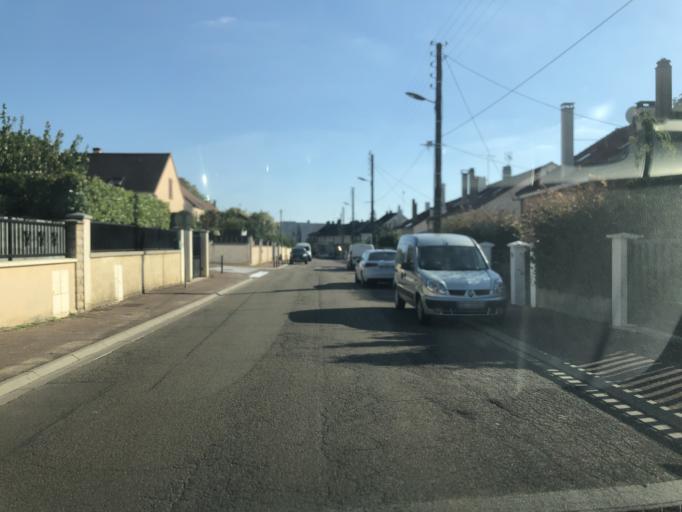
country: FR
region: Bourgogne
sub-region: Departement de l'Yonne
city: Auxerre
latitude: 47.7971
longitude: 3.5889
